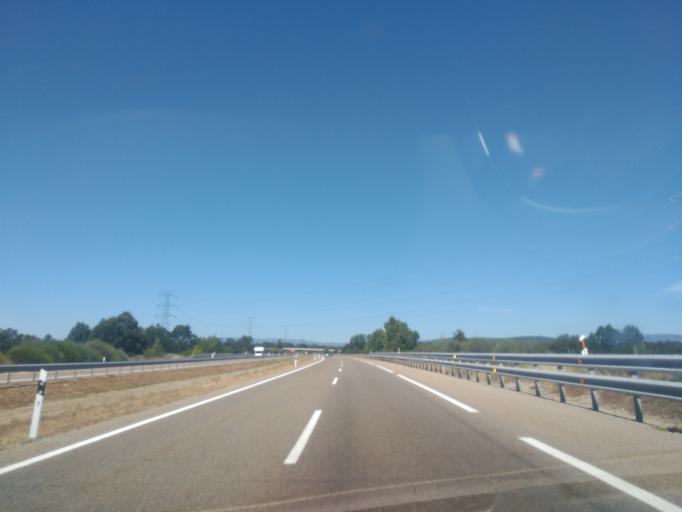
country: ES
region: Castille and Leon
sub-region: Provincia de Zamora
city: Cernadilla
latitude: 42.0282
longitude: -6.4114
